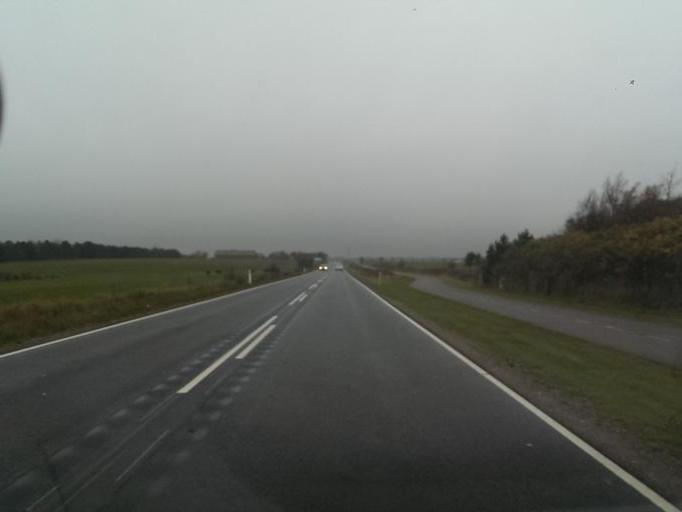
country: DK
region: South Denmark
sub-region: Esbjerg Kommune
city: Tjaereborg
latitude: 55.4633
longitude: 8.5544
